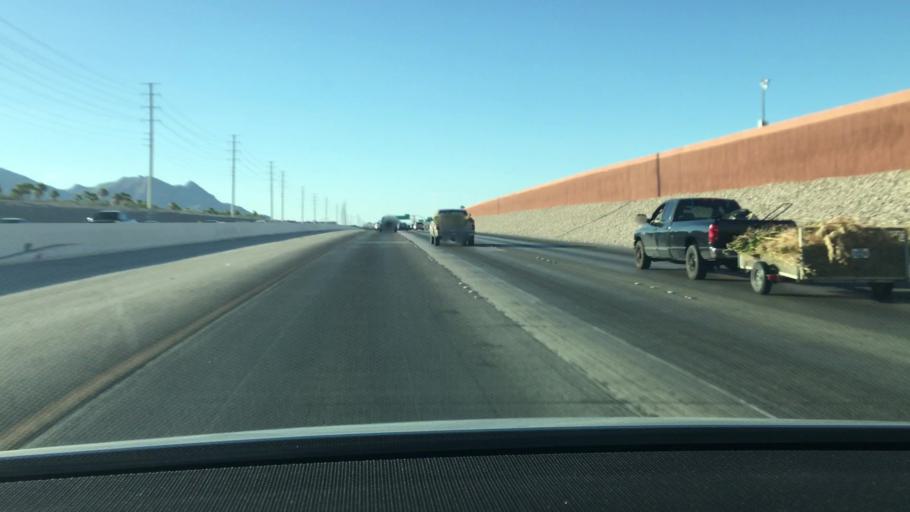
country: US
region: Nevada
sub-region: Clark County
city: Summerlin South
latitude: 36.1351
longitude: -115.3362
